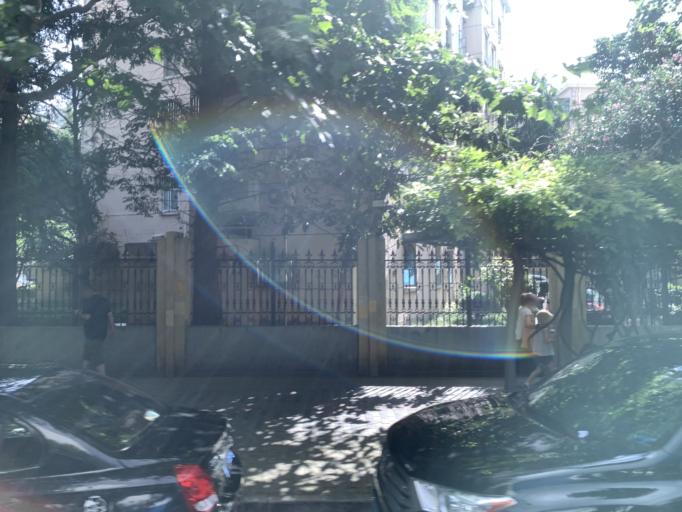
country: CN
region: Shanghai Shi
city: Pudong
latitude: 31.2498
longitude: 121.5592
